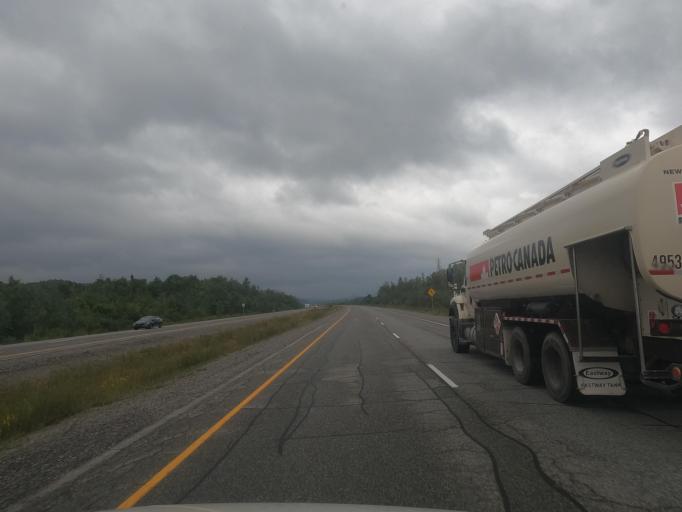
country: CA
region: Ontario
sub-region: Algoma
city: Sault Ste. Marie
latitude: 46.5416
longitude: -84.1316
